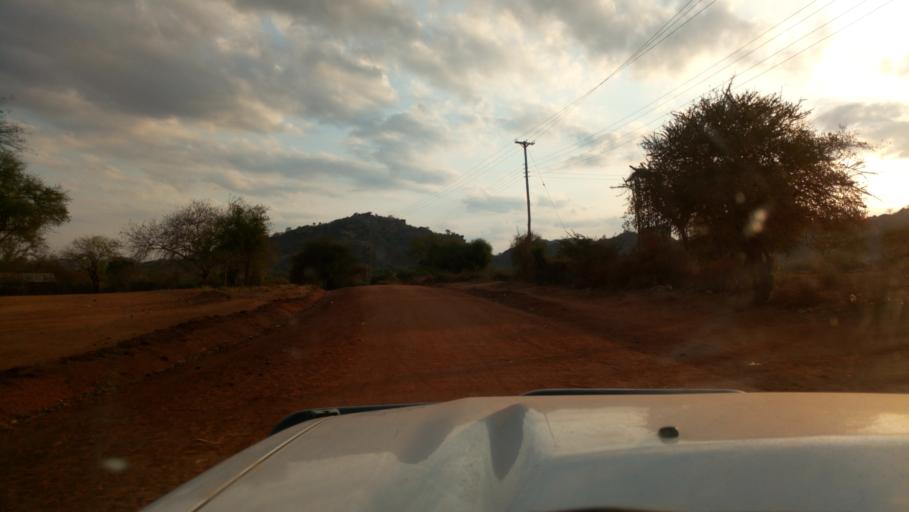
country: KE
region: Kitui
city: Kitui
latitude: -1.6502
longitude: 38.2093
